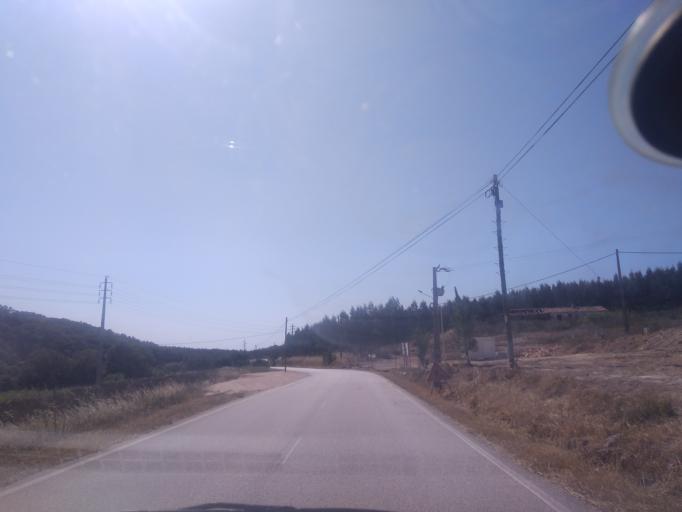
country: PT
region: Faro
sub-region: Aljezur
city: Aljezur
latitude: 37.2187
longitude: -8.7915
